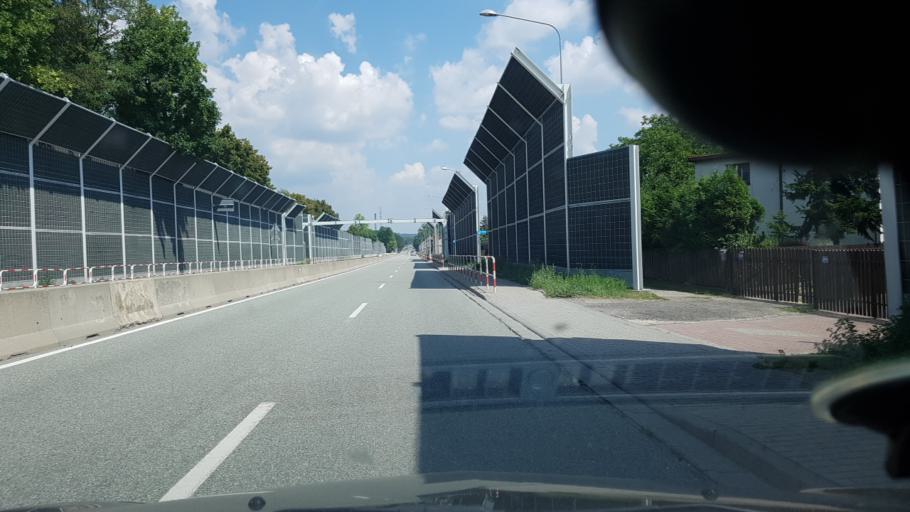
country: PL
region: Silesian Voivodeship
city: Gardawice
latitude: 50.1121
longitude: 18.7991
